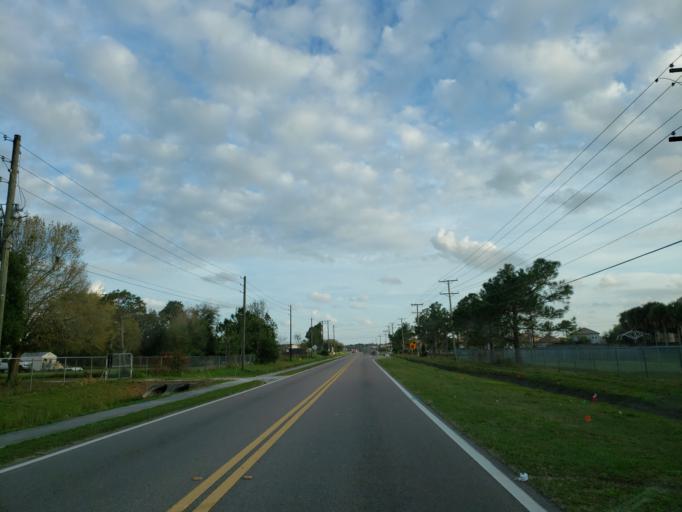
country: US
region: Florida
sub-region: Hillsborough County
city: Balm
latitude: 27.8034
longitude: -82.2883
